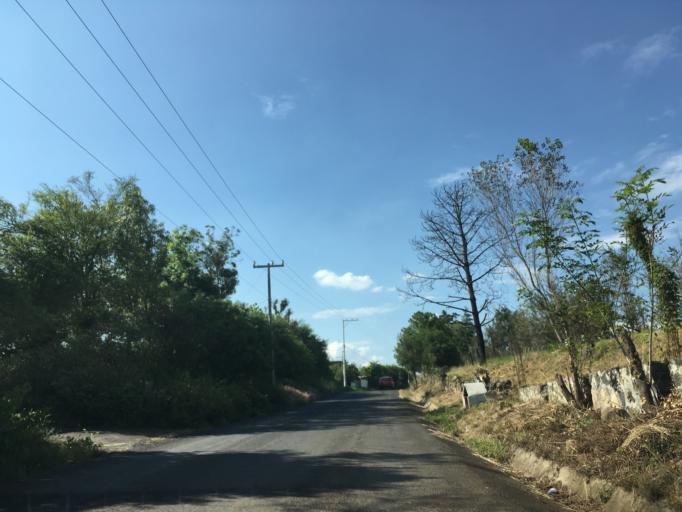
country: MX
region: Michoacan
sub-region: Morelia
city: La Mintzita (Piedra Dura)
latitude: 19.5840
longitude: -101.2734
